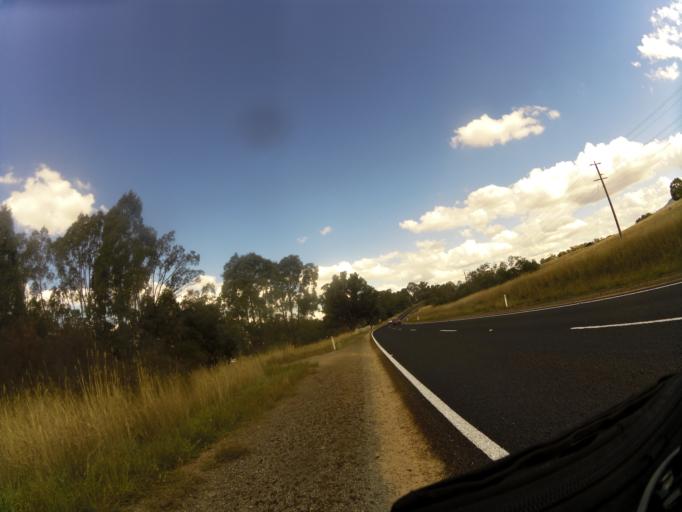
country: AU
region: Victoria
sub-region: Mansfield
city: Mansfield
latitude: -36.9096
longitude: 145.9993
